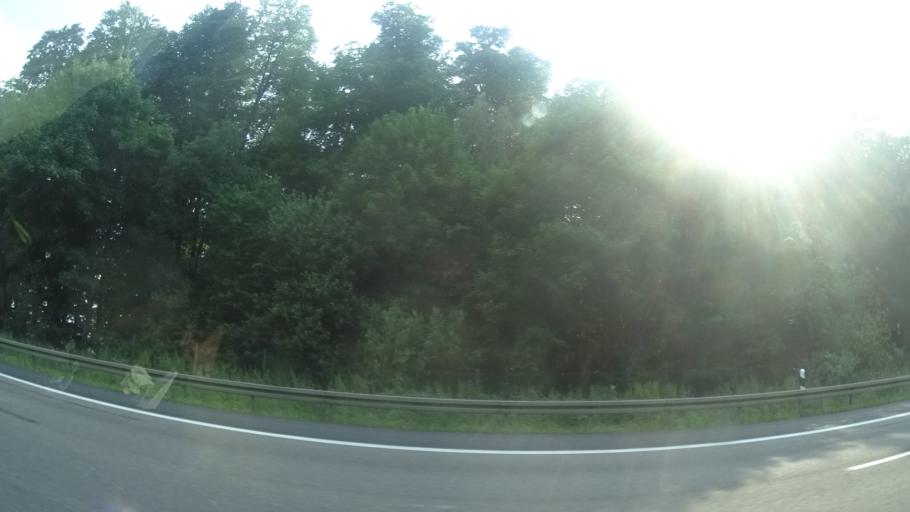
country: DE
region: Hesse
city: Felsberg
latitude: 51.1254
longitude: 9.4767
